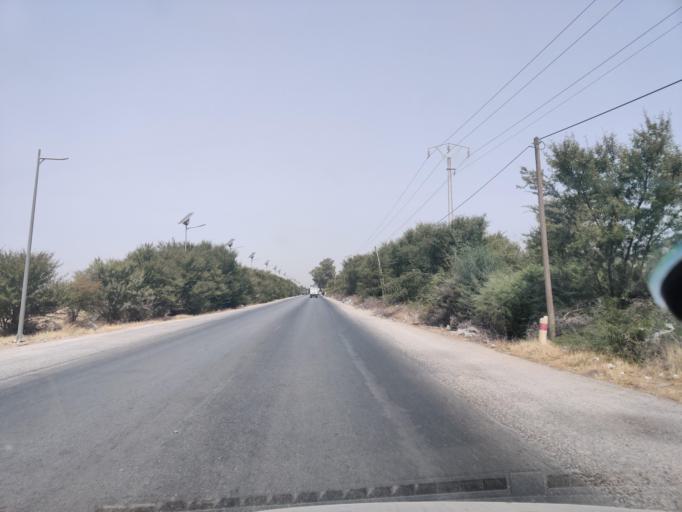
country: TN
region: Tunis
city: La Sebala du Mornag
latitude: 36.6546
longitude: 10.3335
